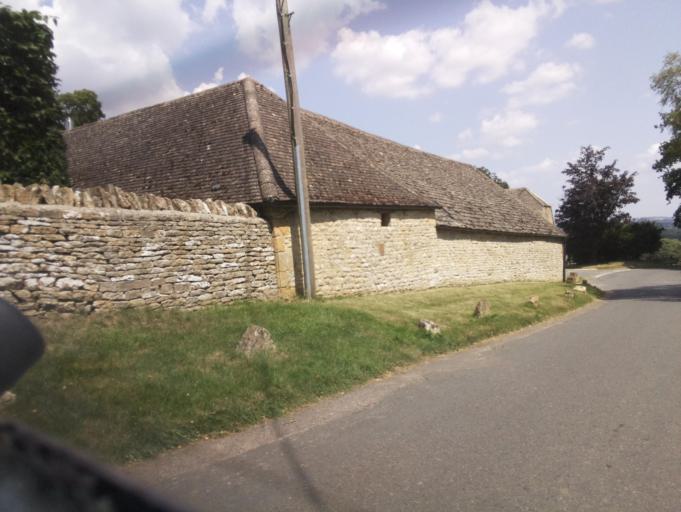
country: GB
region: England
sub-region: Gloucestershire
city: Donnington
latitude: 51.9514
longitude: -1.7193
